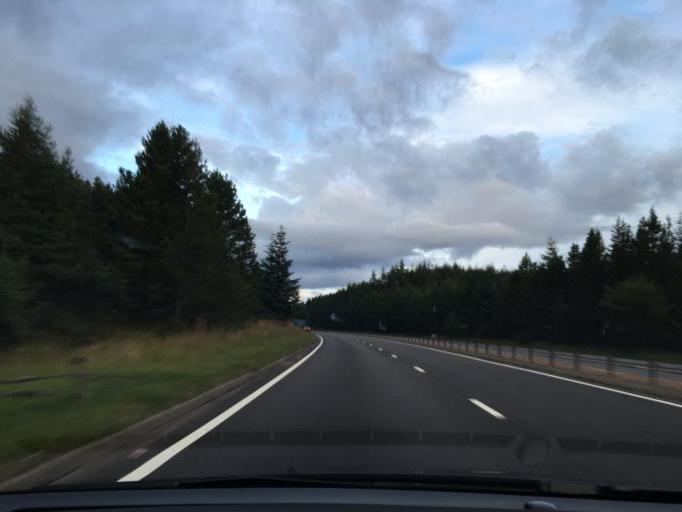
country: GB
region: Scotland
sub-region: Highland
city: Inverness
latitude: 57.3877
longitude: -4.1186
